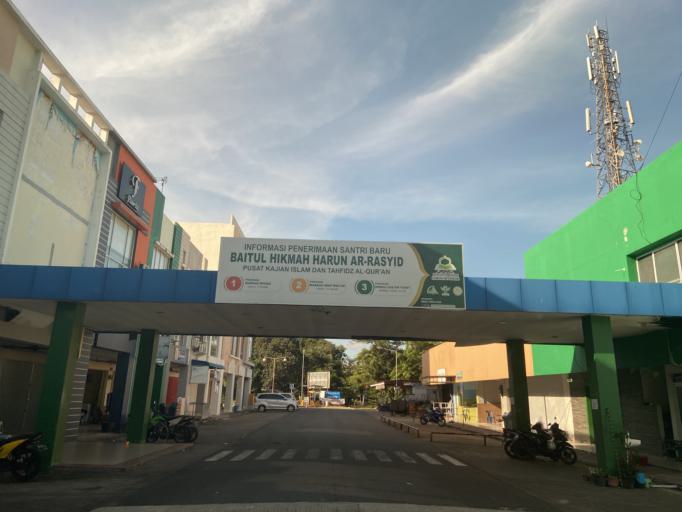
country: SG
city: Singapore
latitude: 1.1056
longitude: 104.0301
